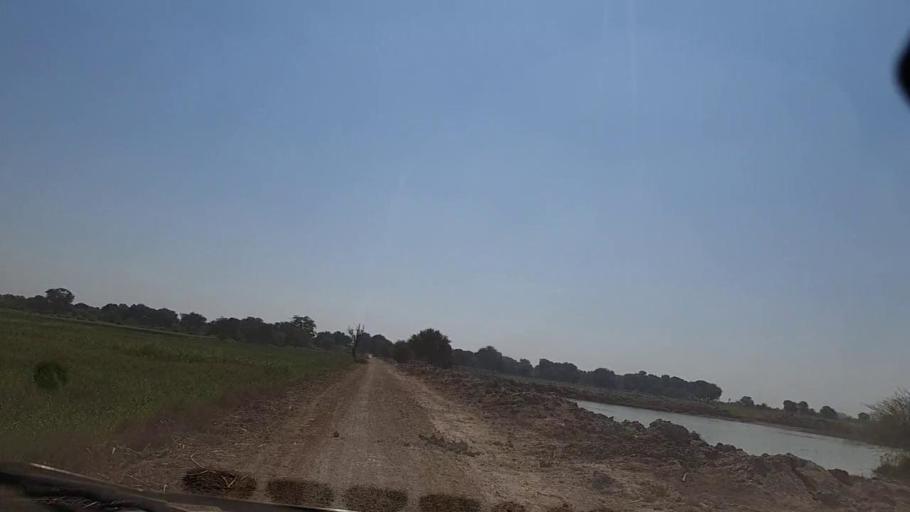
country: PK
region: Sindh
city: Mirpur Khas
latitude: 25.4292
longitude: 69.0559
